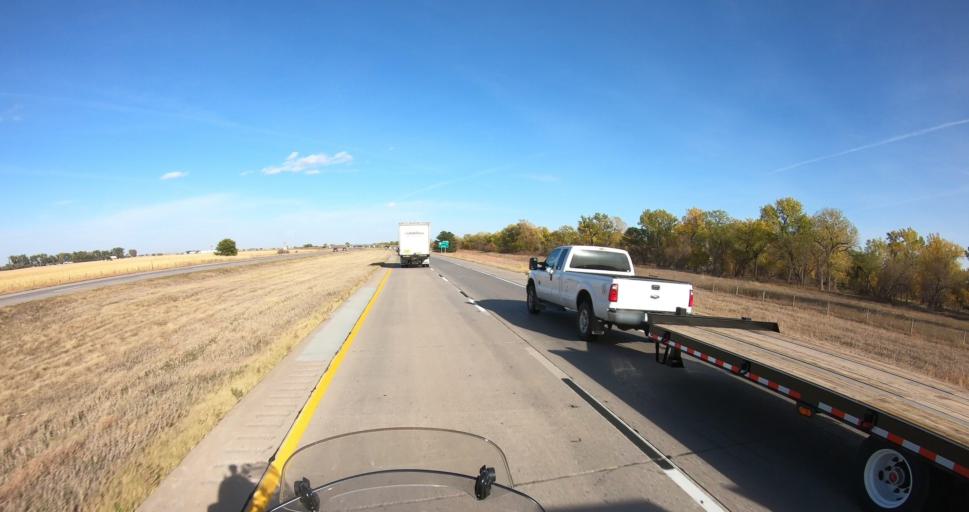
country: US
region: Nebraska
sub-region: Buffalo County
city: Kearney
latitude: 40.6838
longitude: -98.9640
